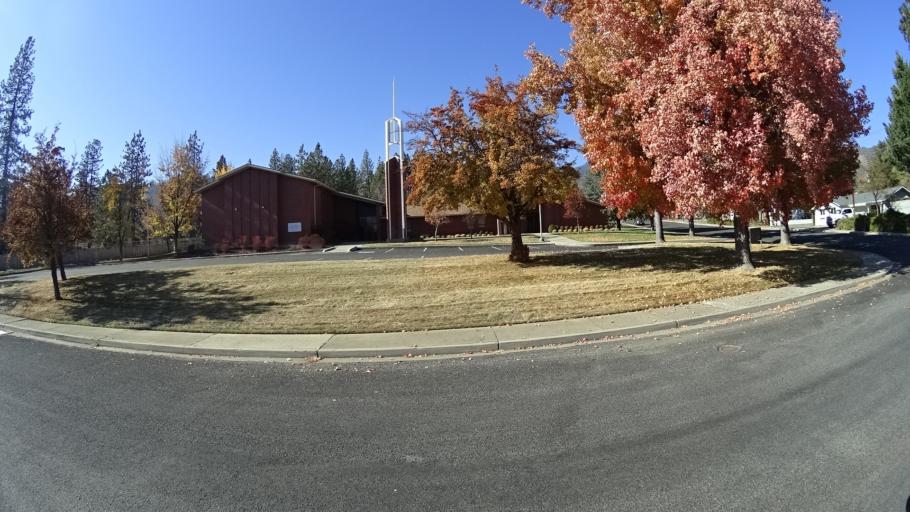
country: US
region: California
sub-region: Siskiyou County
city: Yreka
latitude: 41.7347
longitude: -122.6510
